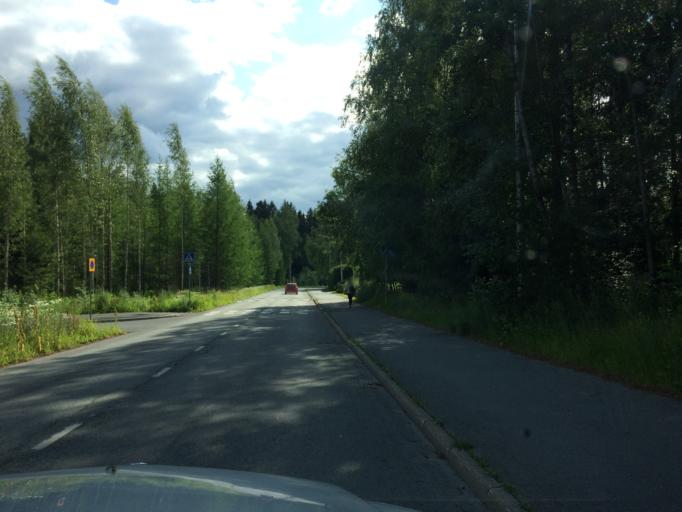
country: FI
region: Haeme
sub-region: Haemeenlinna
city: Haemeenlinna
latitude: 60.9823
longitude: 24.4005
